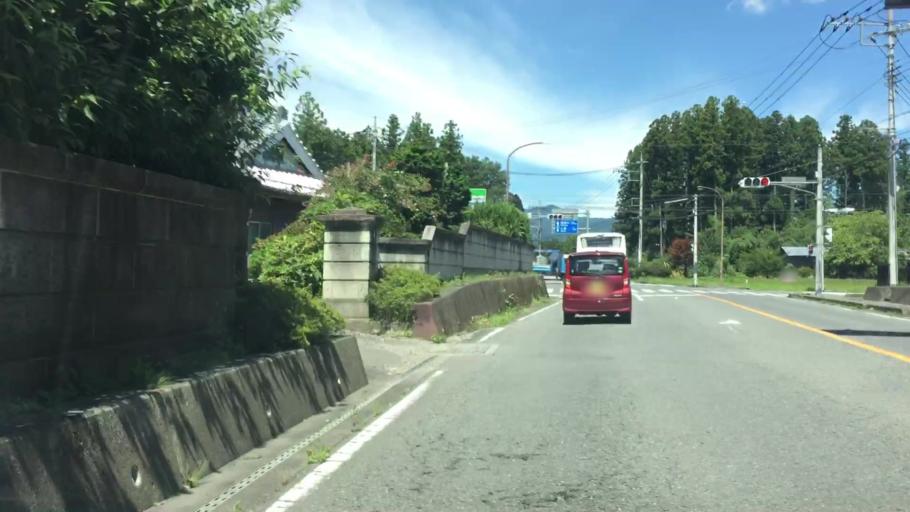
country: JP
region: Tochigi
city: Imaichi
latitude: 36.7489
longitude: 139.7356
